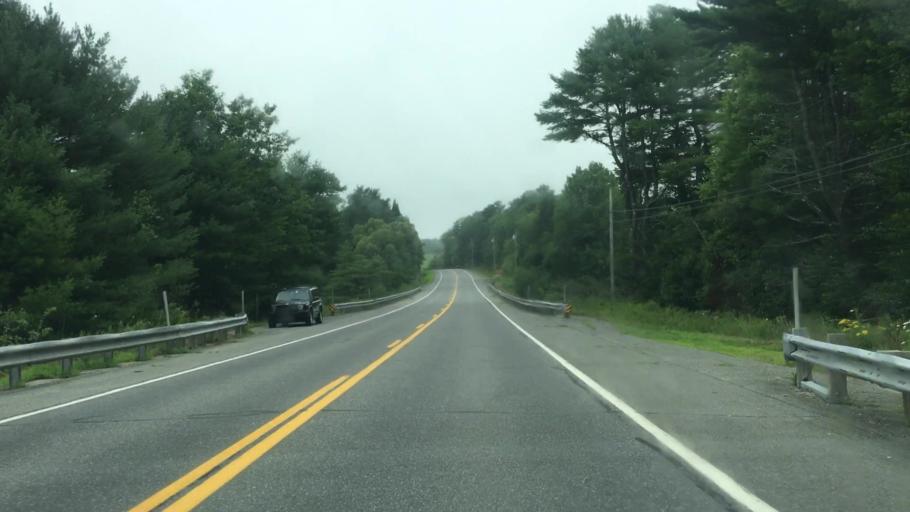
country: US
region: Maine
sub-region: Lincoln County
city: Wiscasset
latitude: 44.0853
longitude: -69.7044
